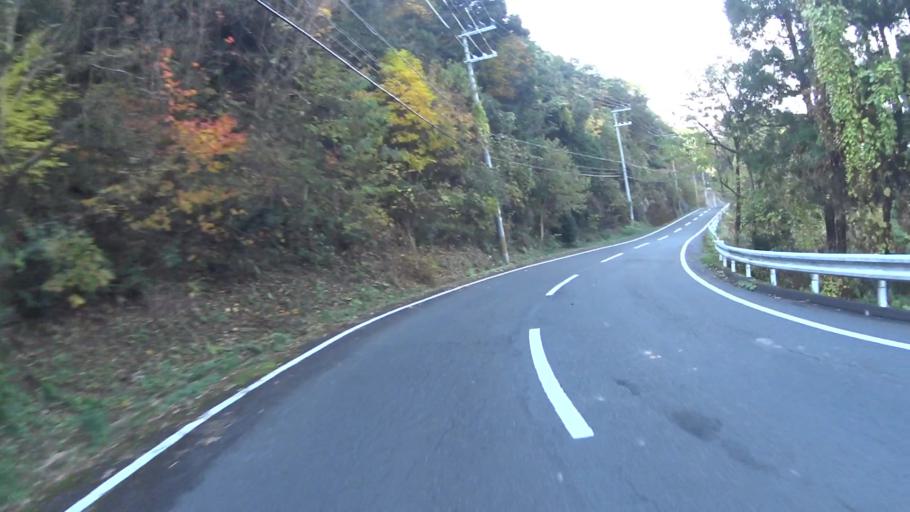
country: JP
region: Kyoto
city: Maizuru
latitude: 35.5424
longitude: 135.3967
